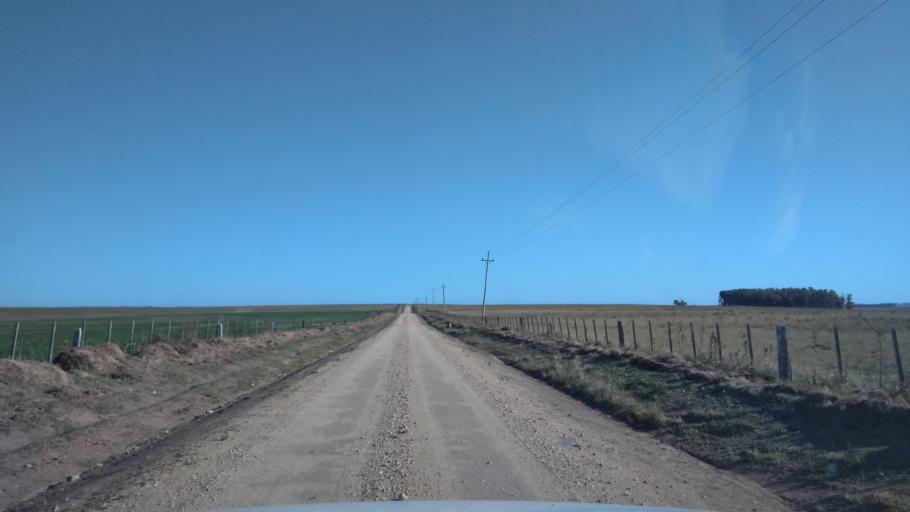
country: UY
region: Florida
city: Casupa
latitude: -34.0125
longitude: -55.7865
